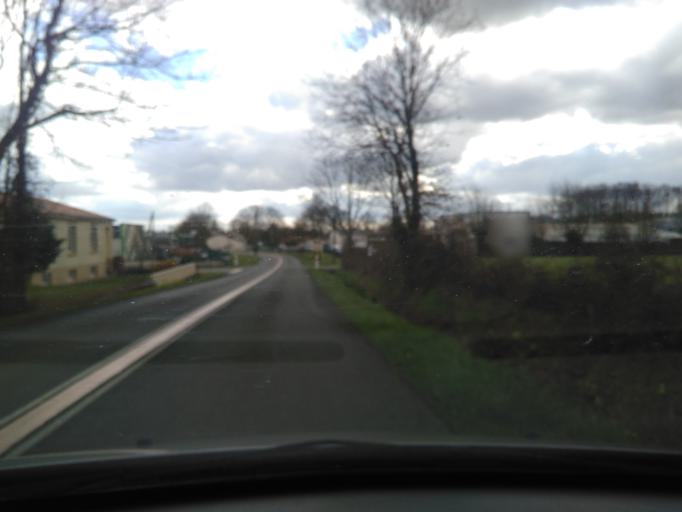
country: FR
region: Pays de la Loire
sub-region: Departement de la Vendee
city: Saint-Martin-des-Noyers
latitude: 46.7317
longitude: -1.1818
